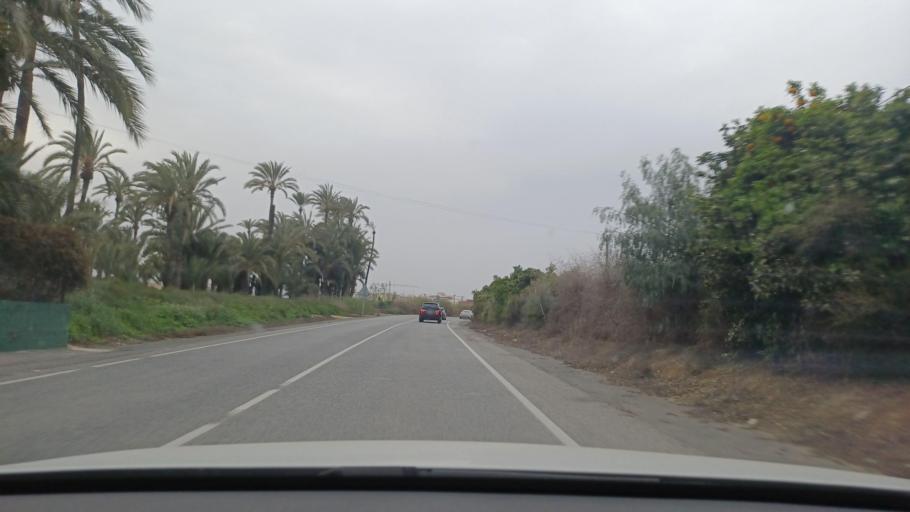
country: ES
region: Valencia
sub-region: Provincia de Alicante
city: Elche
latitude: 38.2467
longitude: -0.6886
